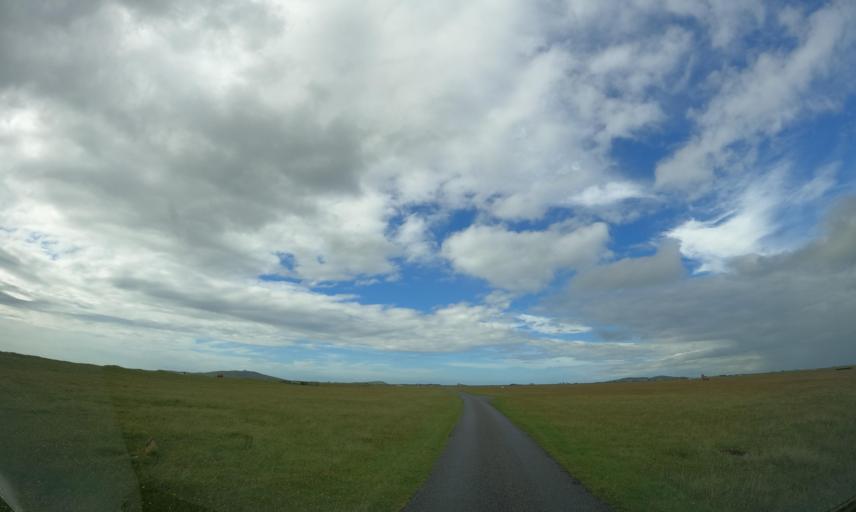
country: GB
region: Scotland
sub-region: Eilean Siar
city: Barra
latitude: 56.4943
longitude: -6.8593
